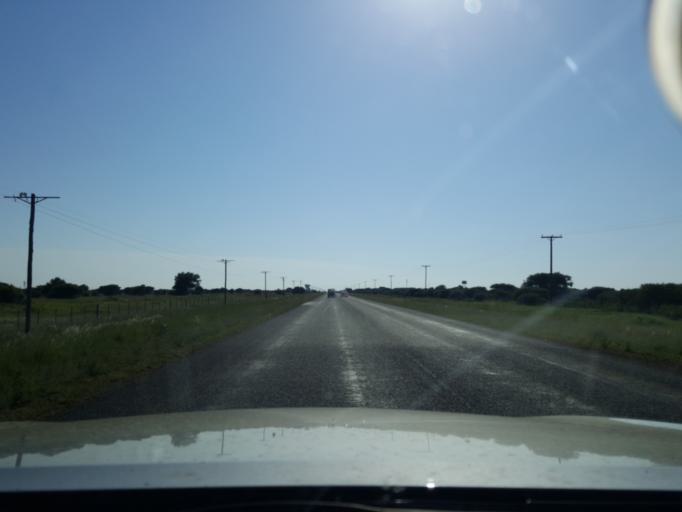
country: ZA
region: North-West
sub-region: Ngaka Modiri Molema District Municipality
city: Mahikeng
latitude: -25.8425
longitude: 25.7244
